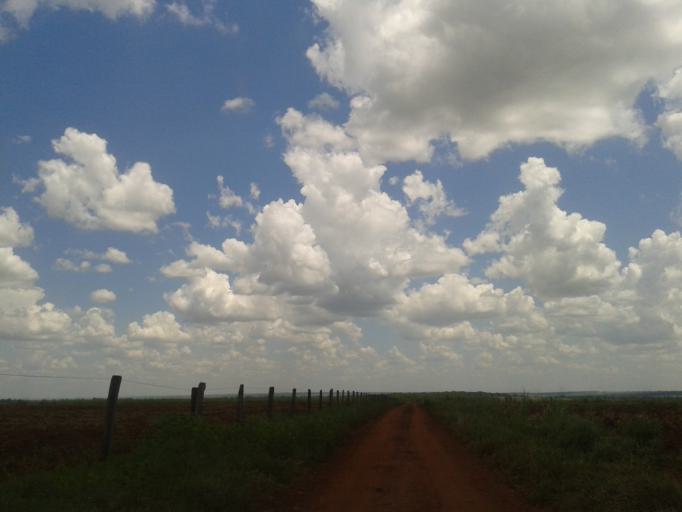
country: BR
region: Minas Gerais
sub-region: Santa Vitoria
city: Santa Vitoria
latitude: -19.1638
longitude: -50.4225
